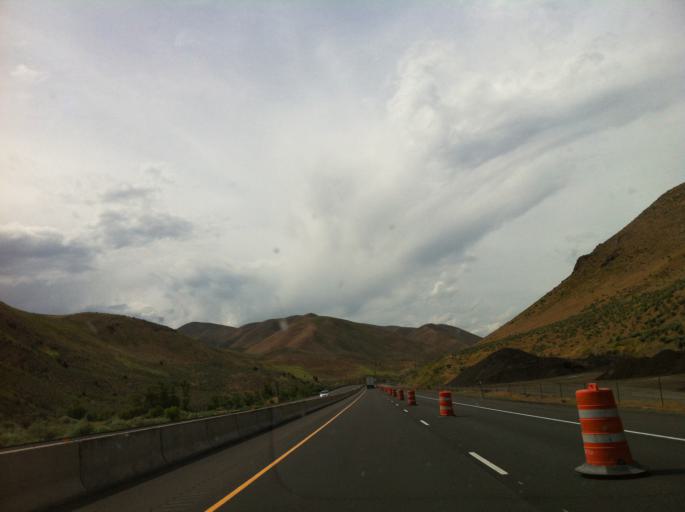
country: US
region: Idaho
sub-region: Washington County
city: Weiser
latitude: 44.3873
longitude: -117.3085
